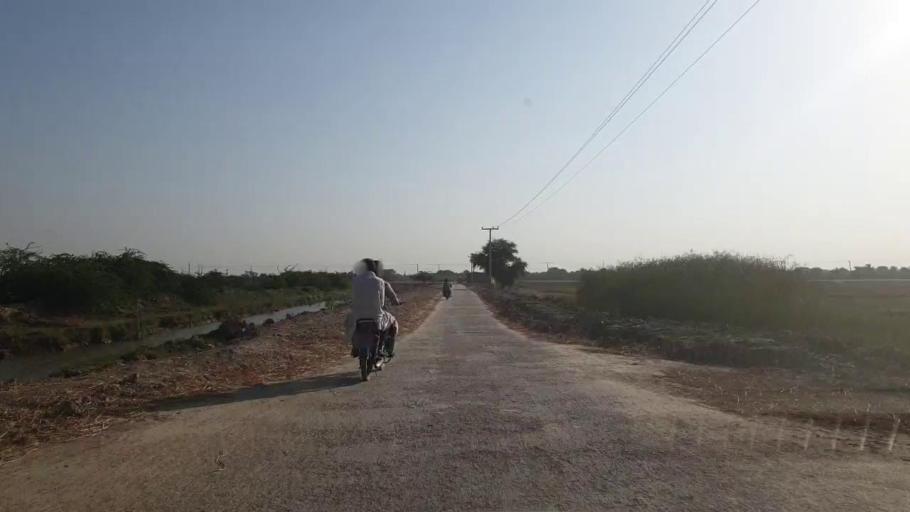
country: PK
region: Sindh
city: Talhar
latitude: 24.9096
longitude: 68.7427
